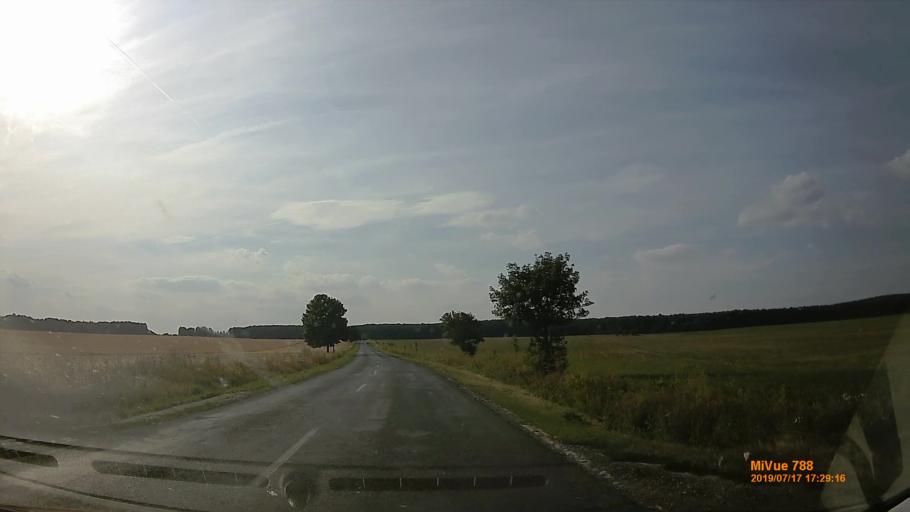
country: HU
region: Veszprem
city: Urkut
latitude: 47.0155
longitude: 17.5867
